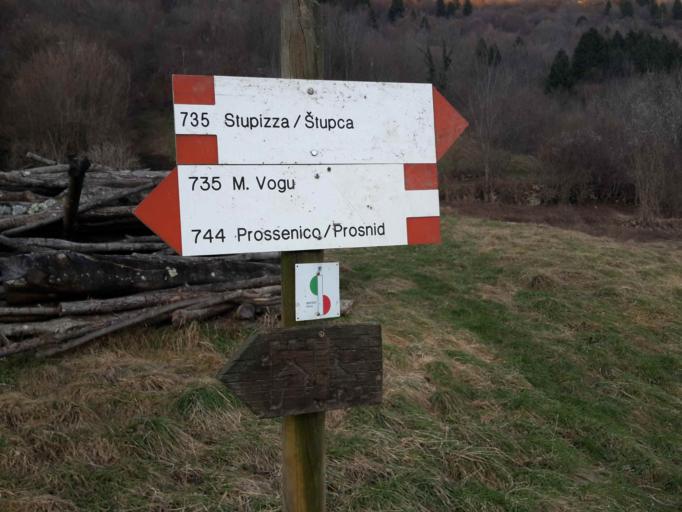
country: IT
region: Friuli Venezia Giulia
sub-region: Provincia di Udine
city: Pulfero
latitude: 46.1987
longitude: 13.4465
